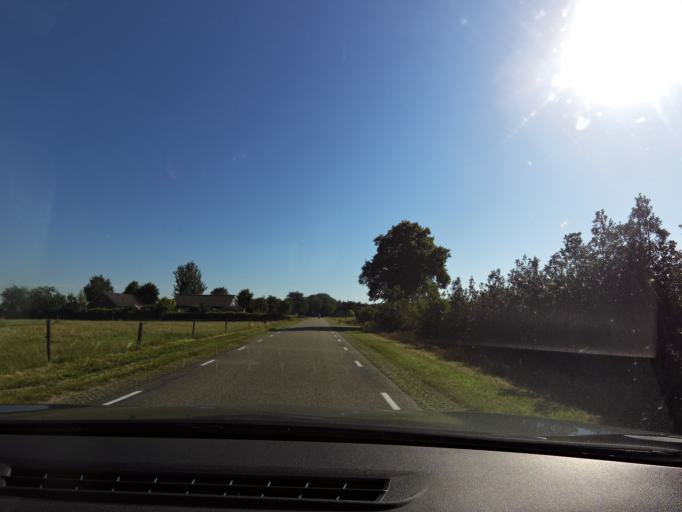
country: NL
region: Overijssel
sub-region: Gemeente Raalte
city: Raalte
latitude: 52.3730
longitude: 6.4033
